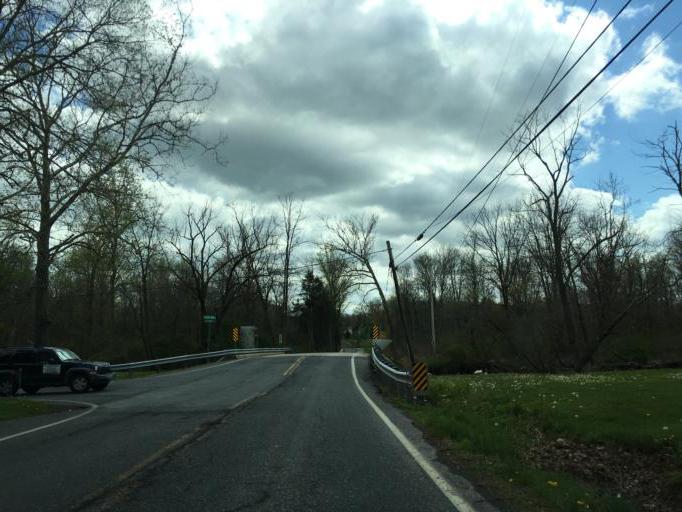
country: US
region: Maryland
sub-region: Frederick County
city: Thurmont
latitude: 39.5944
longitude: -77.3964
